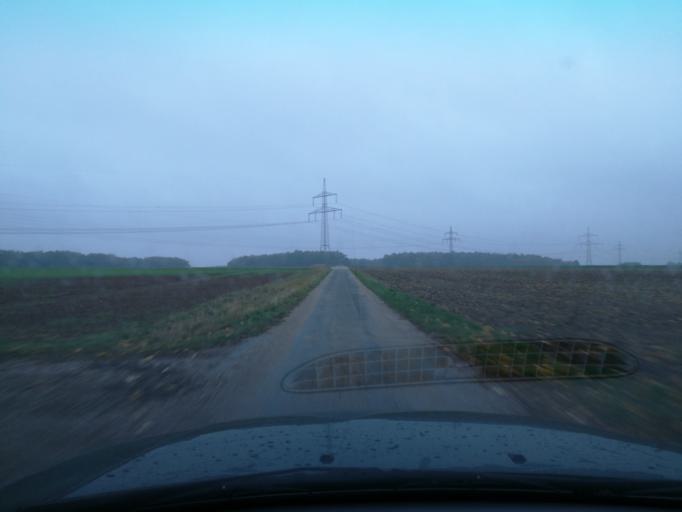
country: DE
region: Bavaria
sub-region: Regierungsbezirk Mittelfranken
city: Obermichelbach
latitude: 49.5383
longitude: 10.9066
